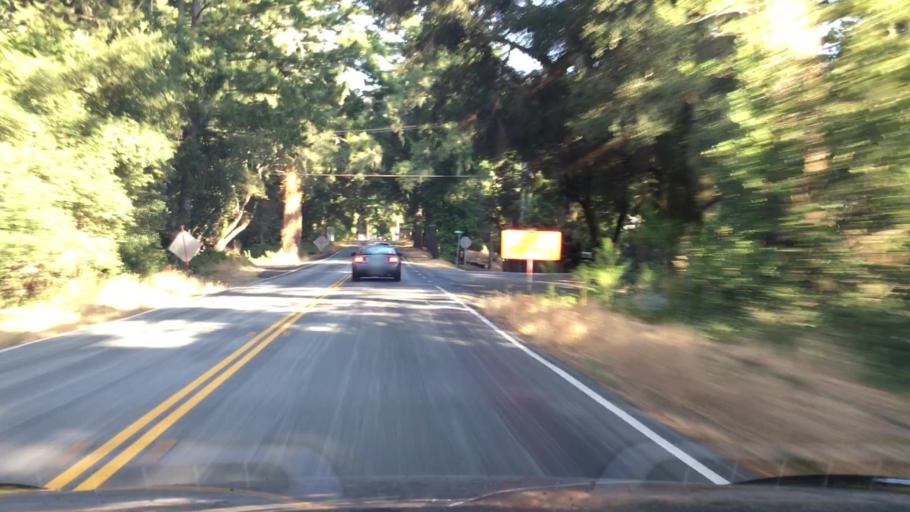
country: US
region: California
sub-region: San Mateo County
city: Portola Valley
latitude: 37.3887
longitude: -122.2678
